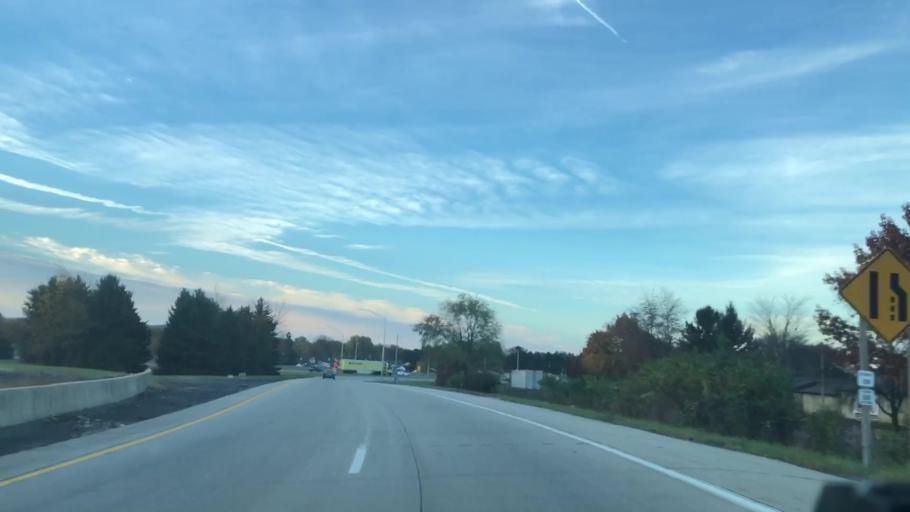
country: US
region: Pennsylvania
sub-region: Lehigh County
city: Fountain Hill
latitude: 40.6492
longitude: -75.4195
